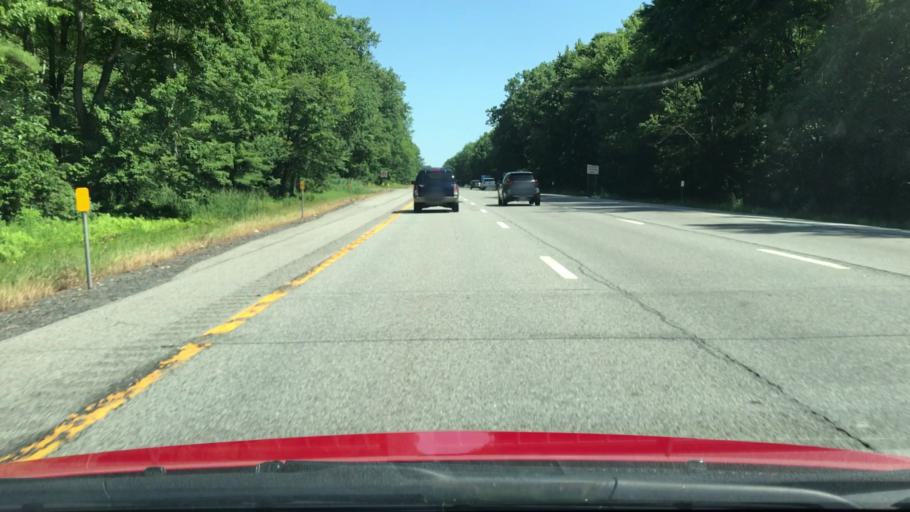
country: US
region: New York
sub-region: Saratoga County
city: Saratoga Springs
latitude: 43.1745
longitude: -73.7098
